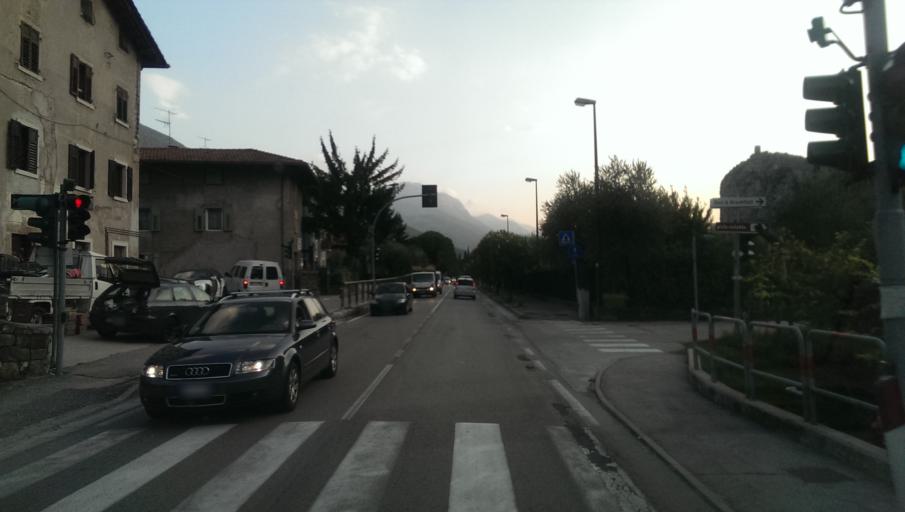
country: IT
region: Trentino-Alto Adige
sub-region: Provincia di Trento
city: Arco
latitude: 45.9316
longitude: 10.8964
